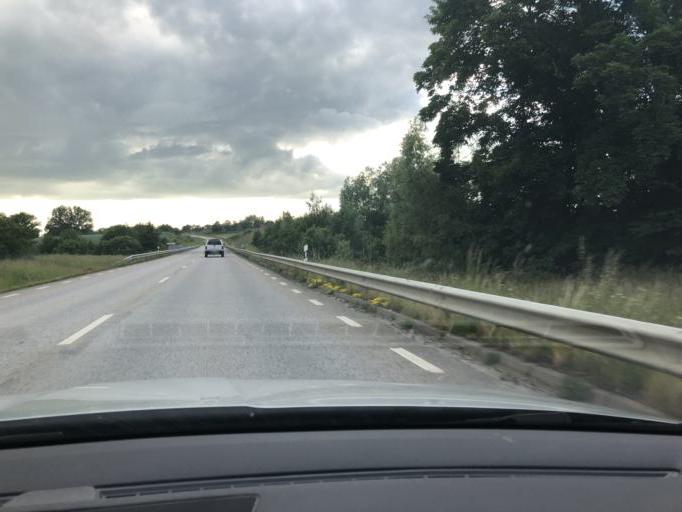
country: SE
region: Skane
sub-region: Simrishamns Kommun
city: Simrishamn
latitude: 55.5355
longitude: 14.2986
